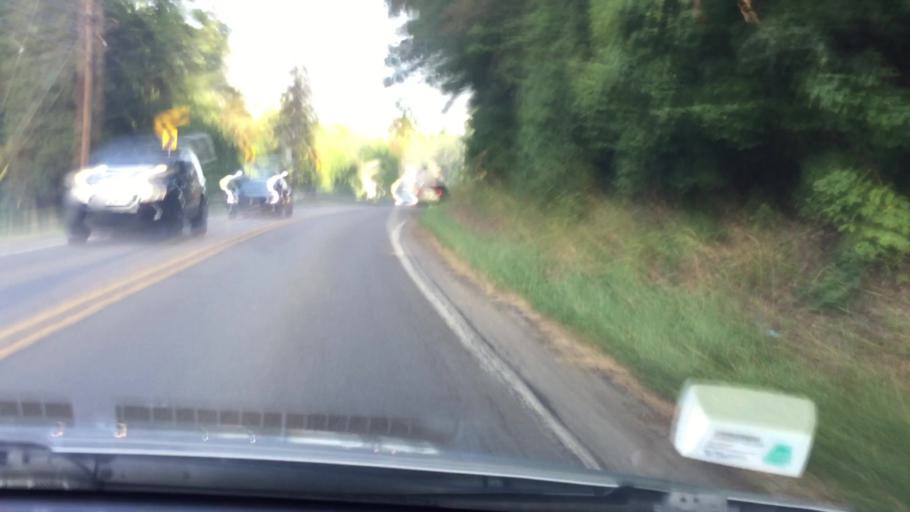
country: US
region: Pennsylvania
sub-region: Allegheny County
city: Franklin Park
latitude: 40.5510
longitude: -80.0911
